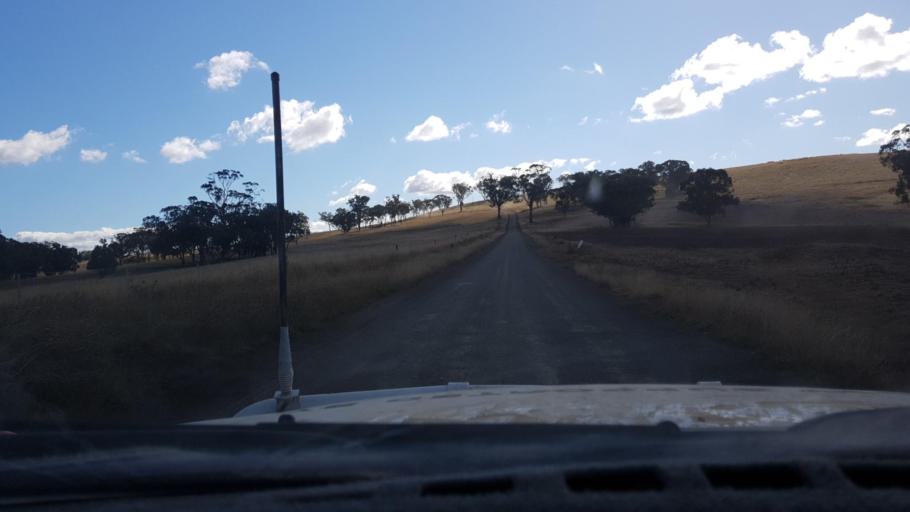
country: AU
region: New South Wales
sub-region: Narrabri
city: Blair Athol
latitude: -30.5548
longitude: 150.4614
